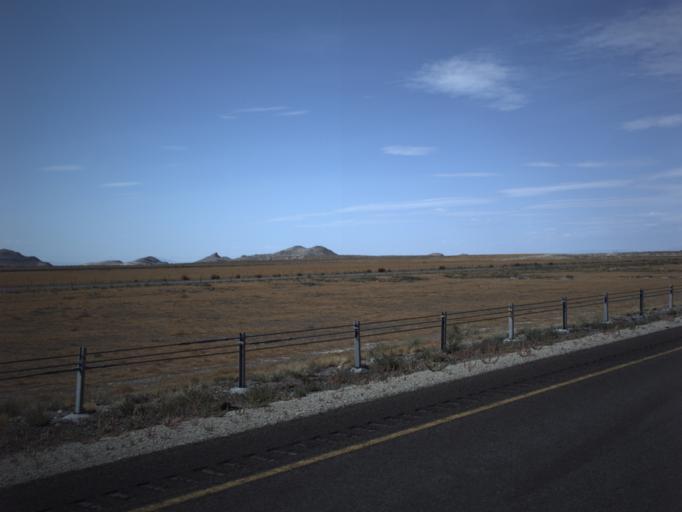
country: US
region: Utah
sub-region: Tooele County
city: Wendover
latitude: 40.7273
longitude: -113.2495
